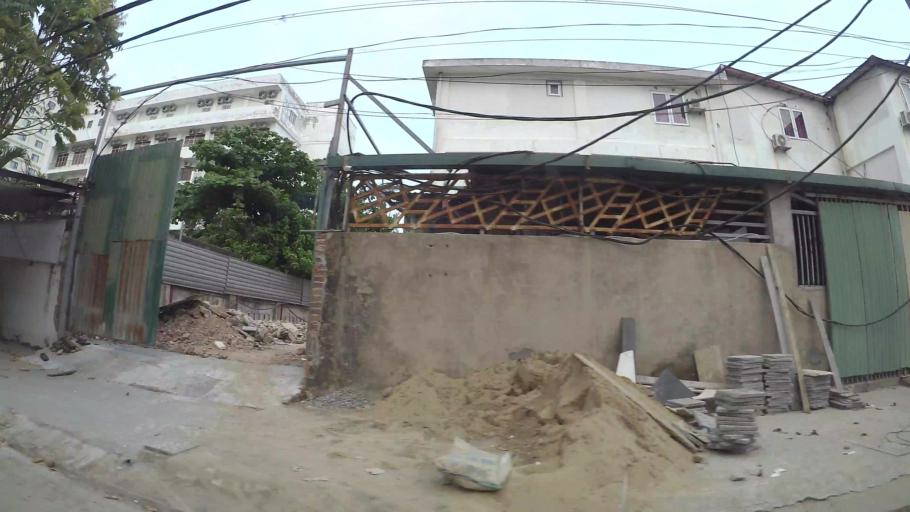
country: VN
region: Da Nang
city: Son Tra
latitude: 16.0568
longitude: 108.2459
